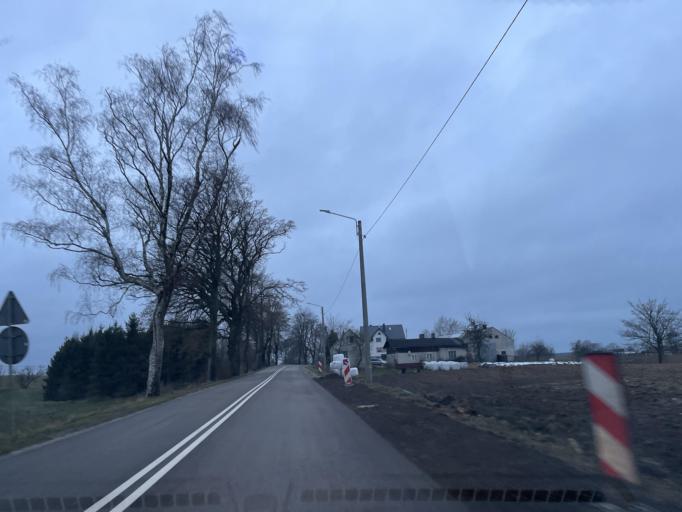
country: PL
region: Pomeranian Voivodeship
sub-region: Powiat kartuski
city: Przodkowo
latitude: 54.4014
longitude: 18.2219
